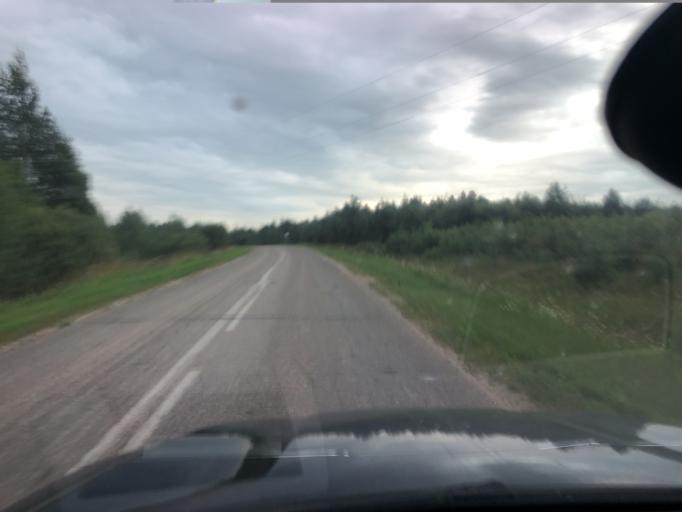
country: RU
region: Jaroslavl
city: Pereslavl'-Zalesskiy
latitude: 57.0134
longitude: 38.9622
